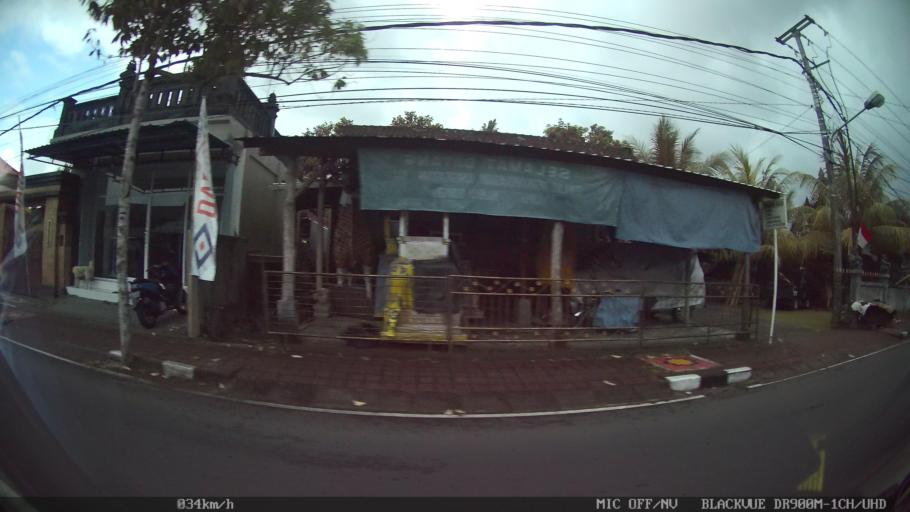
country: ID
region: Bali
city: Banjar Cemenggon
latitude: -8.5319
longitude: 115.2004
